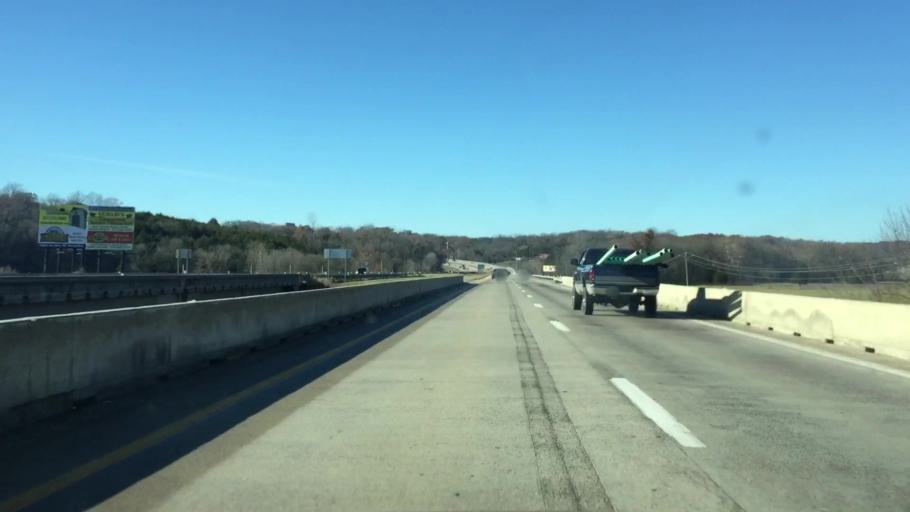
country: US
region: Missouri
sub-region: Cole County
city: Wardsville
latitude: 38.5069
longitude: -92.2555
